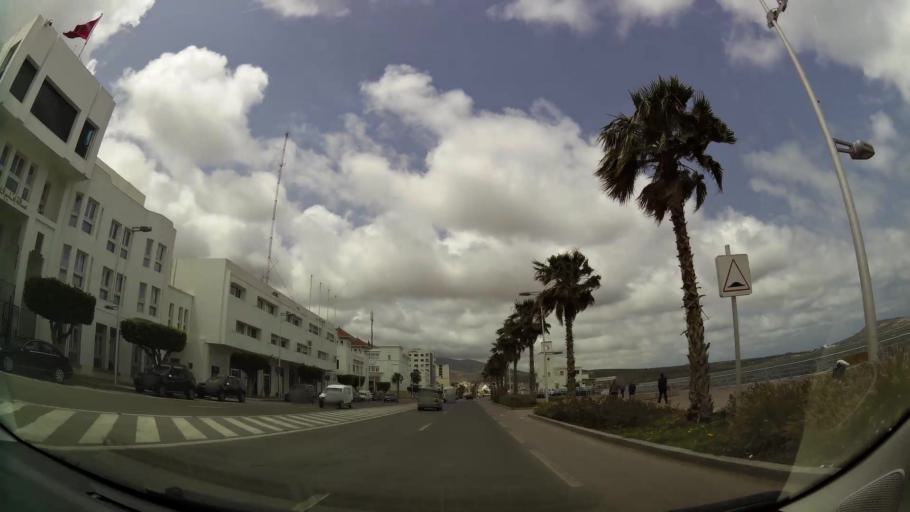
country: MA
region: Oriental
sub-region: Nador
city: Nador
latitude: 35.1801
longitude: -2.9221
